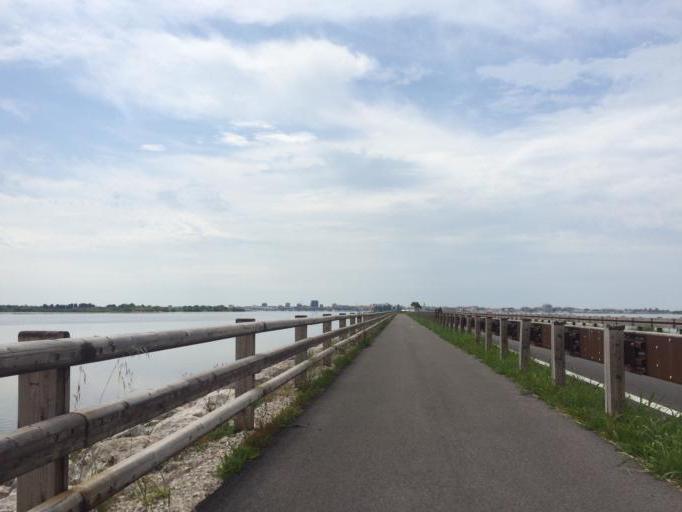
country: IT
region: Friuli Venezia Giulia
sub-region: Provincia di Gorizia
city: Grado
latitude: 45.7010
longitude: 13.3832
